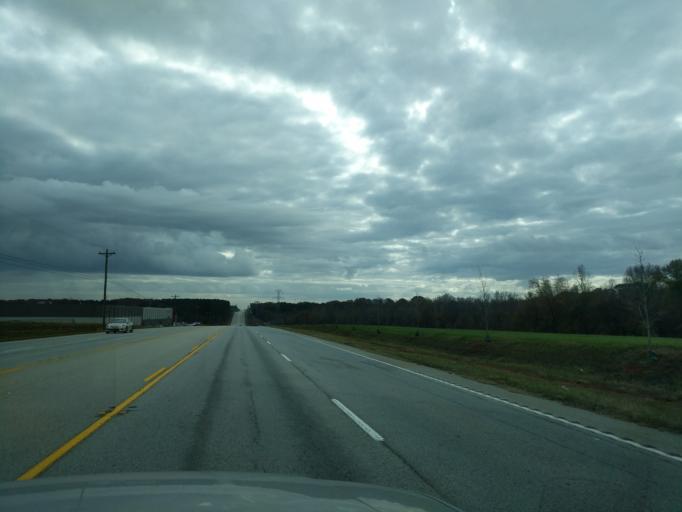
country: US
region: South Carolina
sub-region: Spartanburg County
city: Roebuck
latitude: 34.8696
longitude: -82.0324
